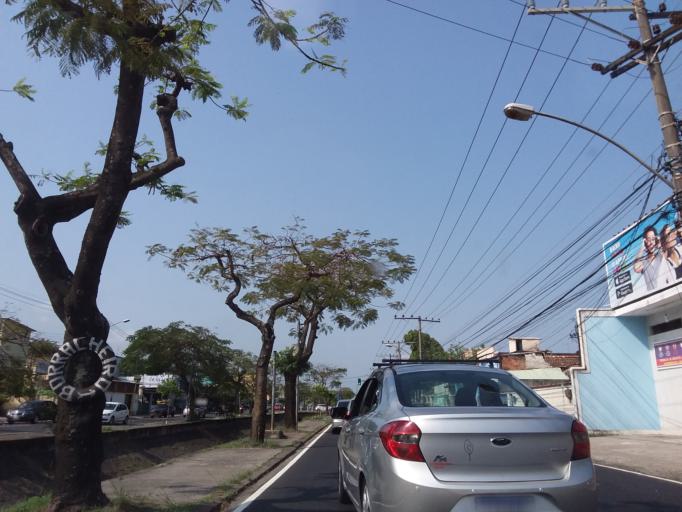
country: BR
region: Rio de Janeiro
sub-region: Nilopolis
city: Nilopolis
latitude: -22.9002
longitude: -43.5428
